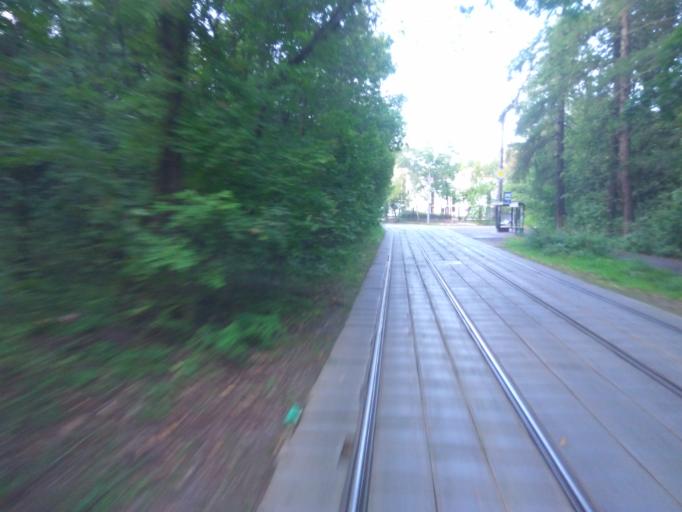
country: RU
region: Moscow
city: Sokol'niki
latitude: 55.8053
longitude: 37.6913
